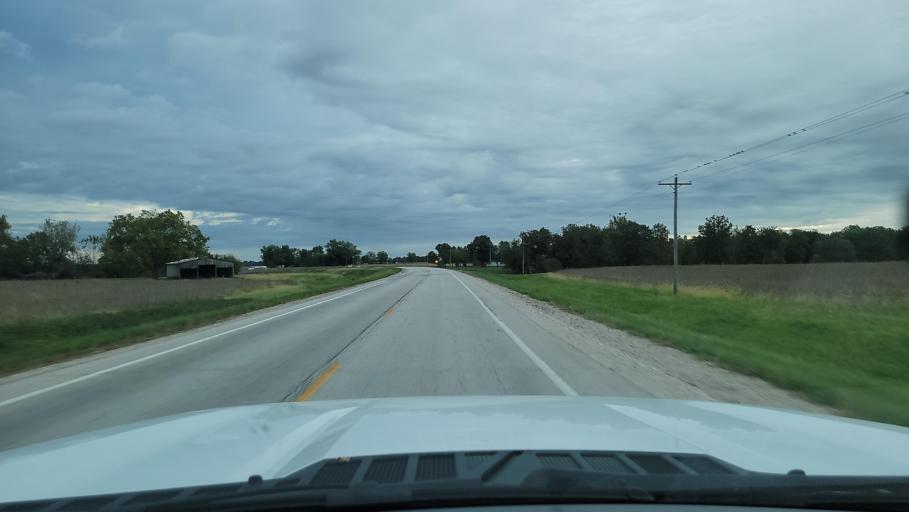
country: US
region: Illinois
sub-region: Schuyler County
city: Rushville
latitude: 40.0808
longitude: -90.6128
